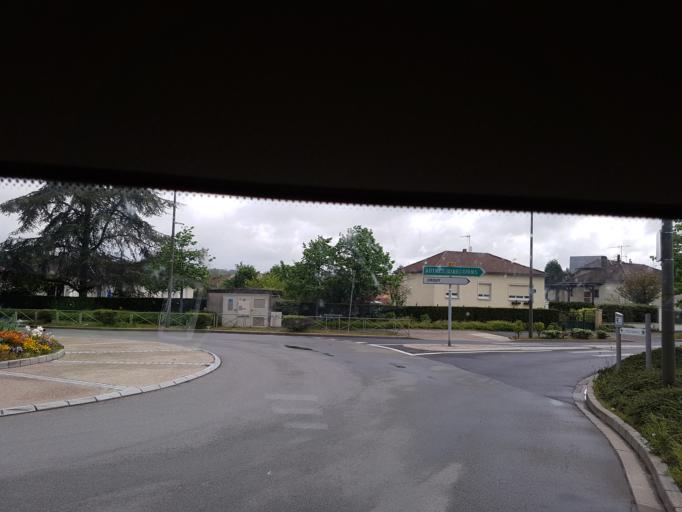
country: FR
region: Picardie
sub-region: Departement de l'Aisne
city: Soissons
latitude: 49.3926
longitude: 3.3328
